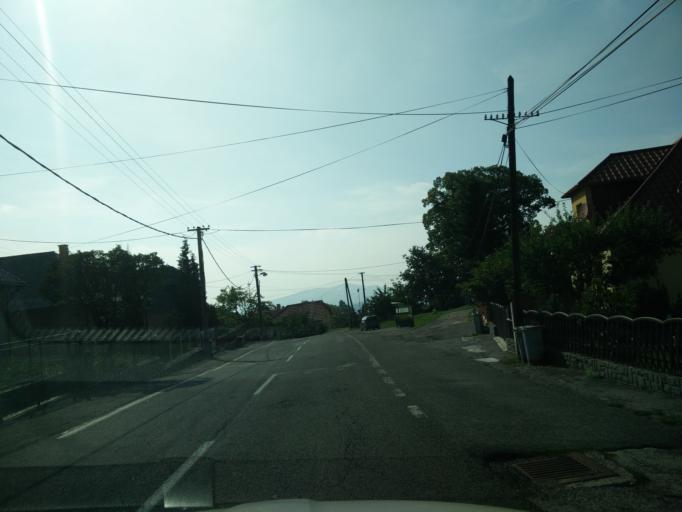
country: SK
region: Nitriansky
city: Prievidza
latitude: 48.6846
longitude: 18.6296
